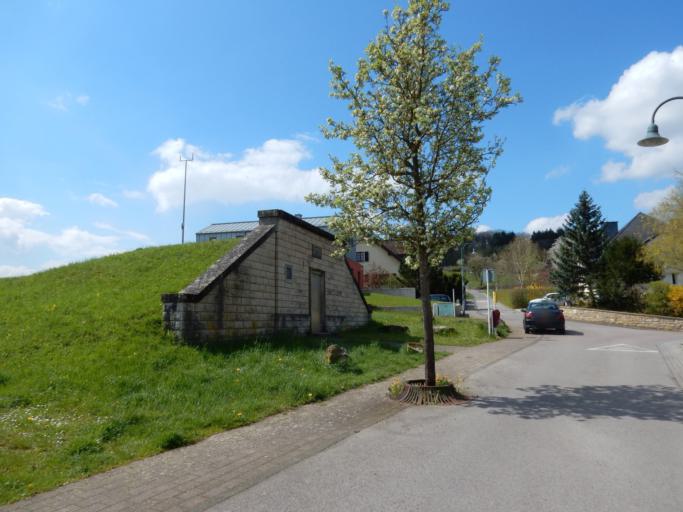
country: LU
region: Grevenmacher
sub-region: Canton de Grevenmacher
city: Grevenmacher
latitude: 49.6811
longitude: 6.4358
